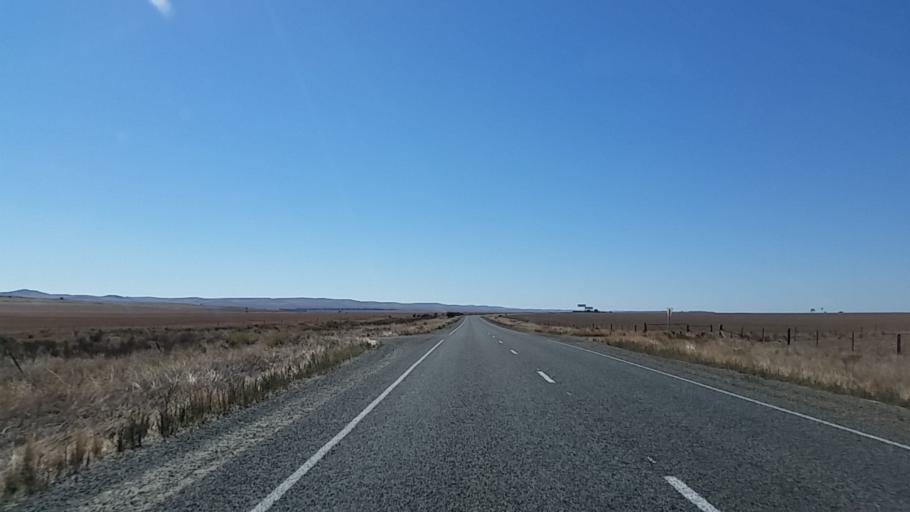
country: AU
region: South Australia
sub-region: Northern Areas
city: Jamestown
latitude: -33.2749
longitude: 138.8684
